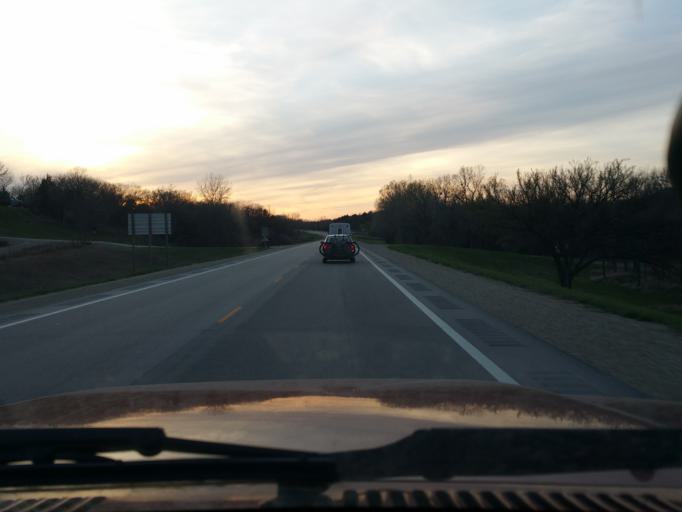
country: US
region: Kansas
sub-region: Riley County
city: Manhattan
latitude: 39.2485
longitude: -96.6313
